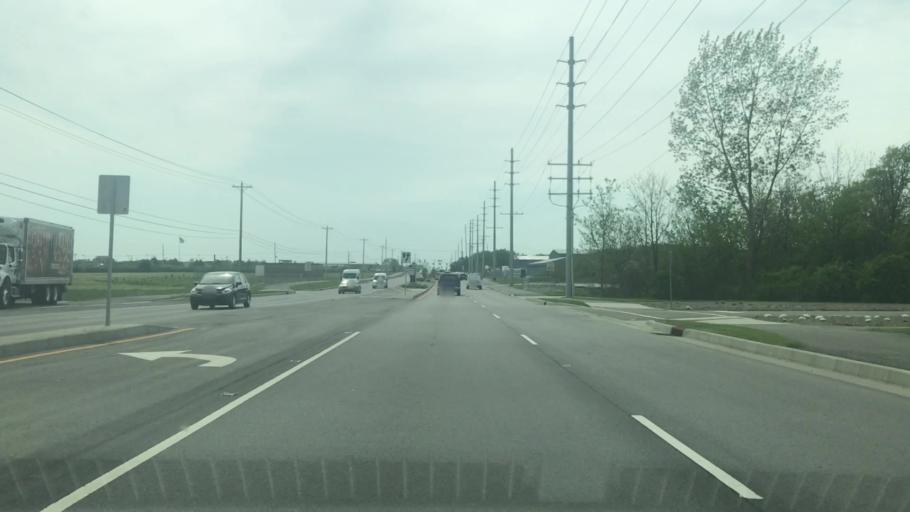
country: US
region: Indiana
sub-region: Johnson County
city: New Whiteland
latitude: 39.5868
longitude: -86.0946
